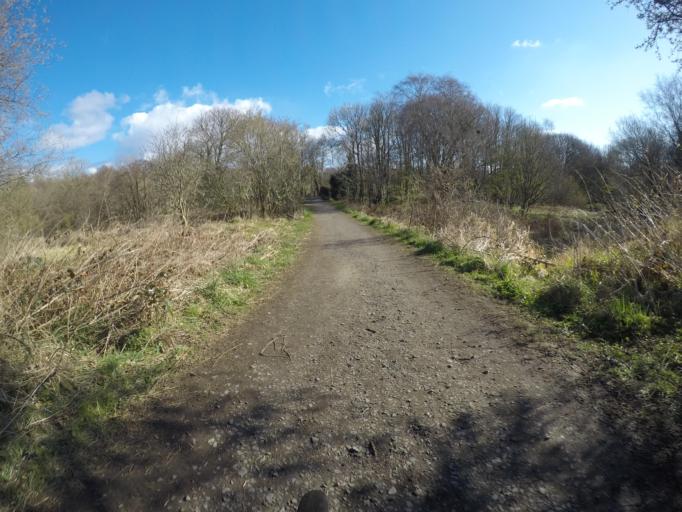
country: GB
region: Scotland
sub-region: North Ayrshire
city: Irvine
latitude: 55.6470
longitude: -4.6600
